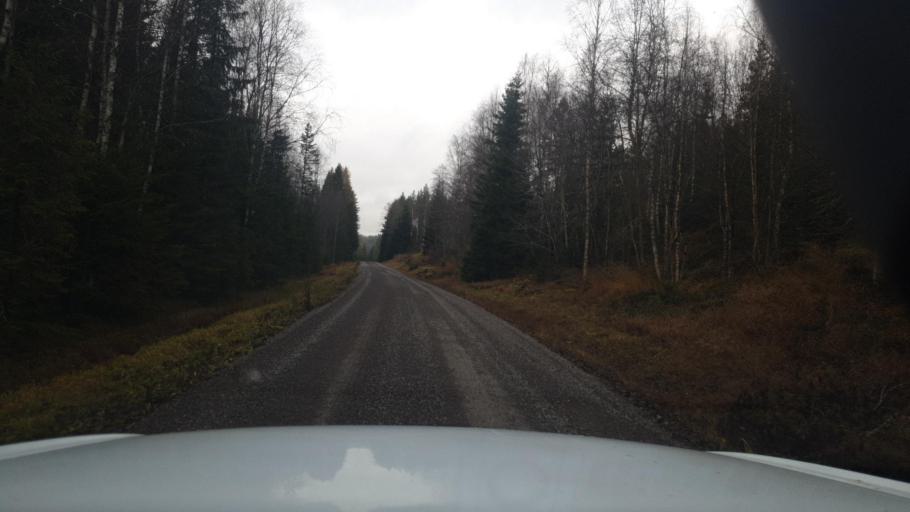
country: SE
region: Vaermland
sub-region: Eda Kommun
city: Charlottenberg
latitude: 60.0517
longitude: 12.6299
